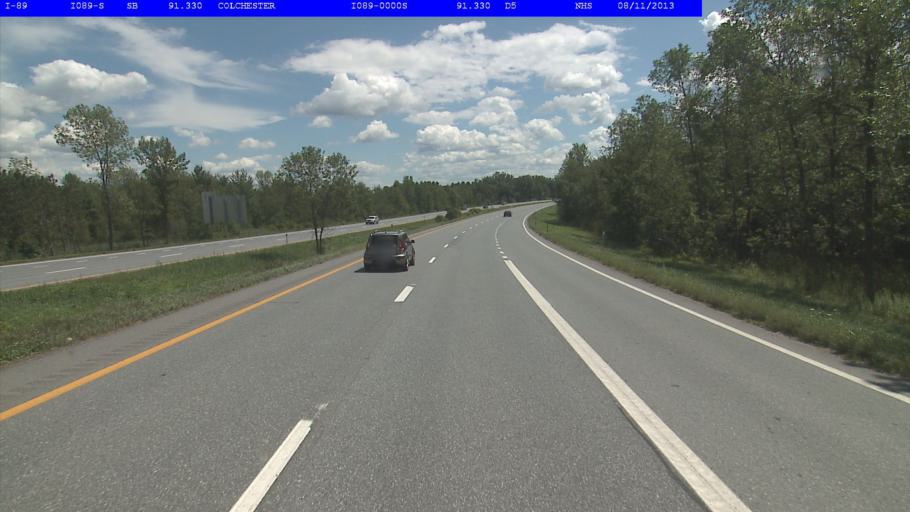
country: US
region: Vermont
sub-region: Chittenden County
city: Winooski
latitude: 44.5044
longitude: -73.1785
